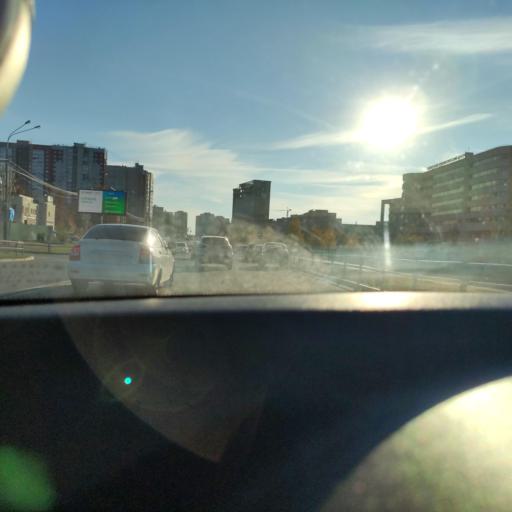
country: RU
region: Samara
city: Samara
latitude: 53.2635
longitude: 50.2105
